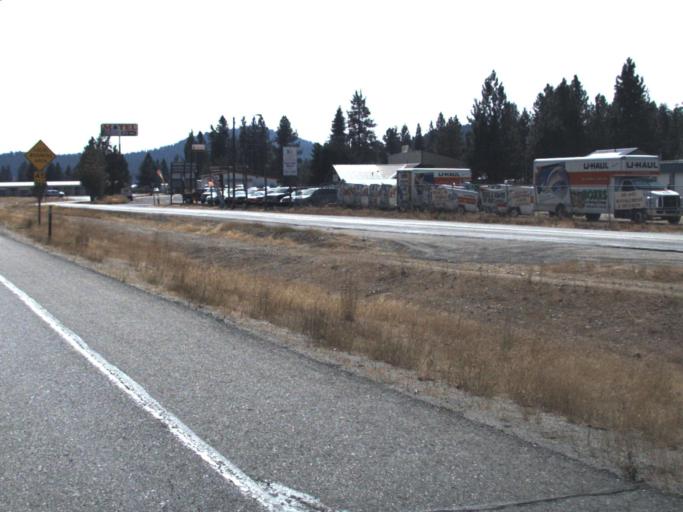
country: US
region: Washington
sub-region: Spokane County
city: Deer Park
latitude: 48.0622
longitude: -117.6217
